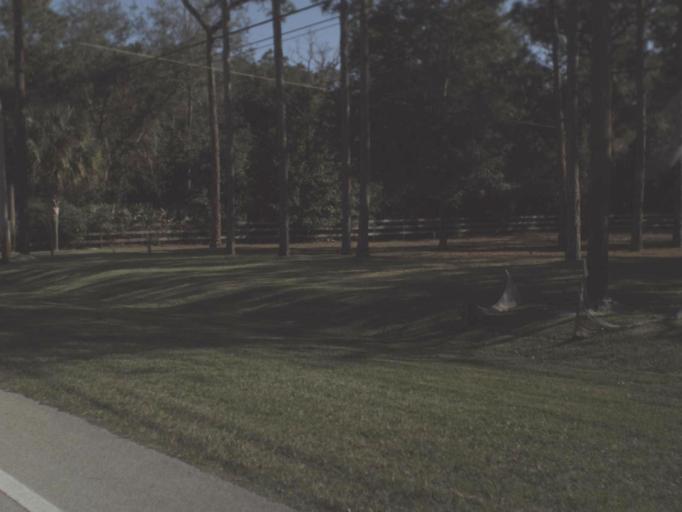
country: US
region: Florida
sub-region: Volusia County
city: Samsula-Spruce Creek
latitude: 29.0843
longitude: -81.0604
